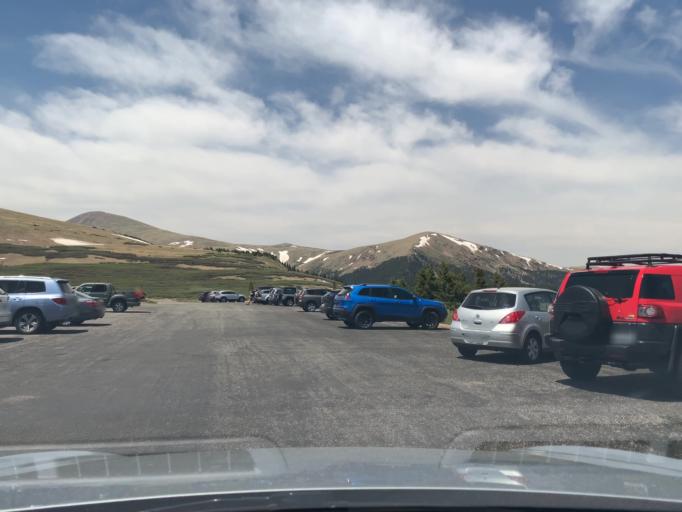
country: US
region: Colorado
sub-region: Clear Creek County
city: Georgetown
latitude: 39.5970
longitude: -105.7120
